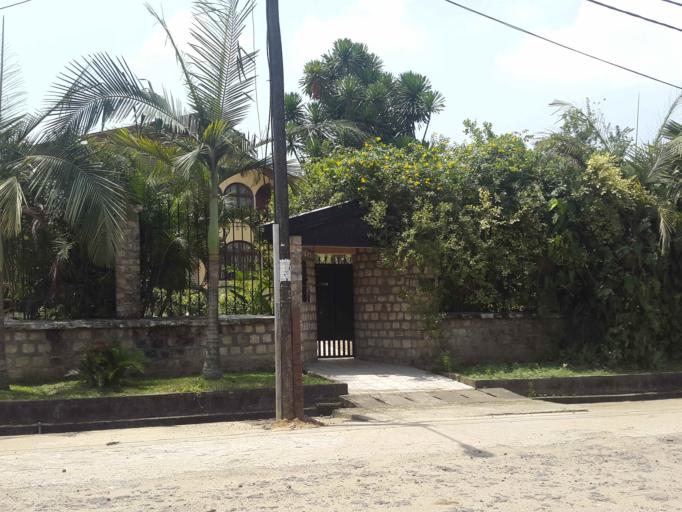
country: CM
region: Littoral
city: Douala
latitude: 4.0932
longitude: 9.7328
